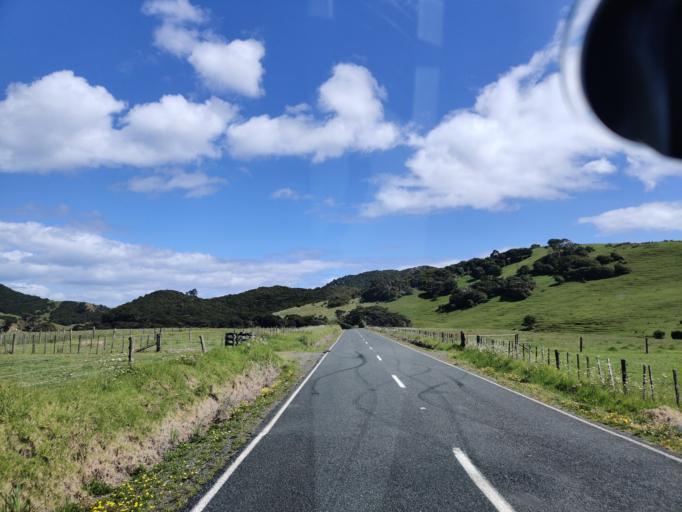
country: NZ
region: Northland
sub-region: Far North District
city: Paihia
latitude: -35.2713
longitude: 174.2790
